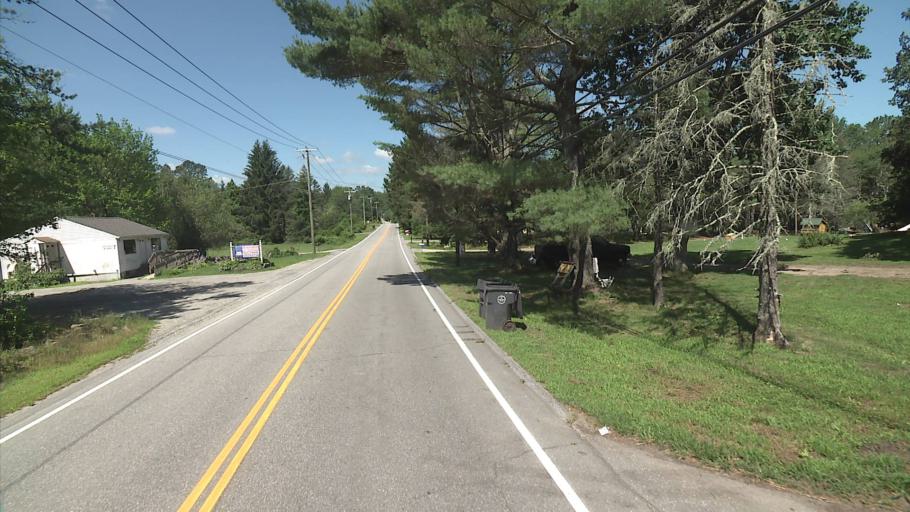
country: US
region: Connecticut
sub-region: Windham County
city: Moosup
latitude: 41.6919
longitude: -71.8196
